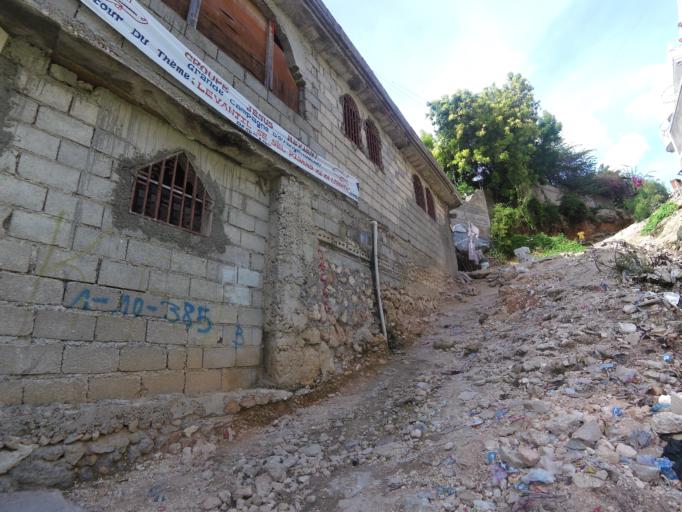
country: HT
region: Ouest
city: Port-au-Prince
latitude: 18.5245
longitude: -72.3359
